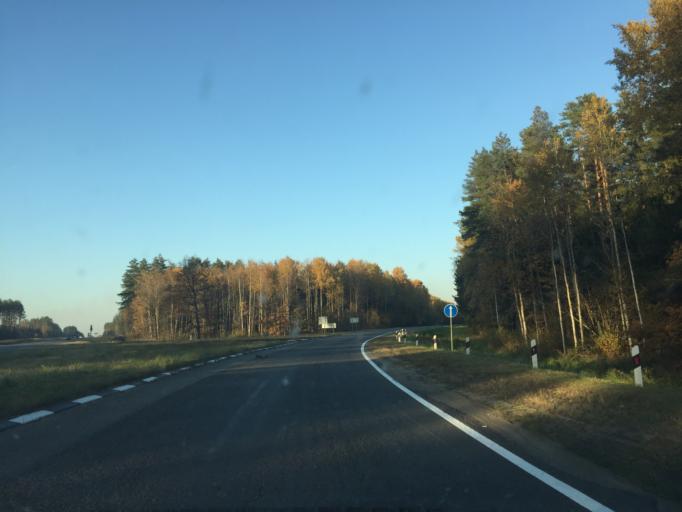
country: BY
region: Mogilev
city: Poselok Voskhod
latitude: 53.7659
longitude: 30.3646
